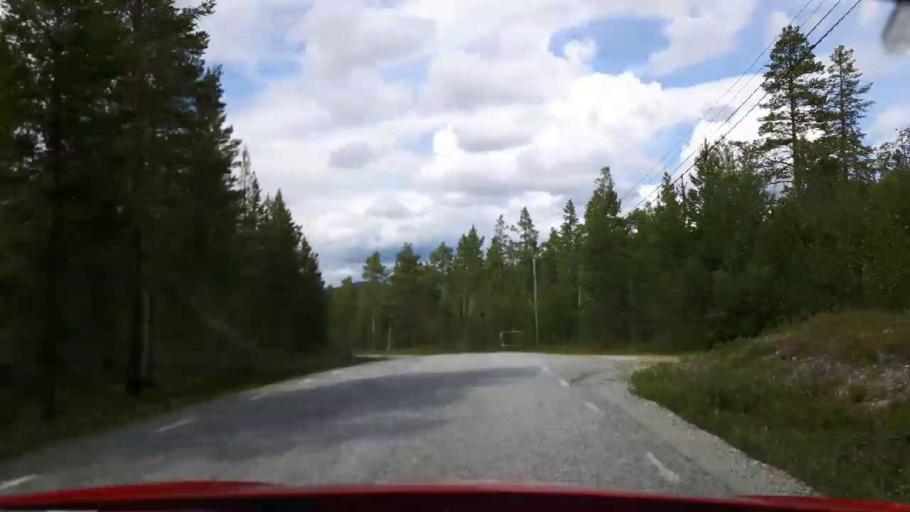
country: NO
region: Hedmark
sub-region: Engerdal
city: Engerdal
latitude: 62.4215
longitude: 12.6916
